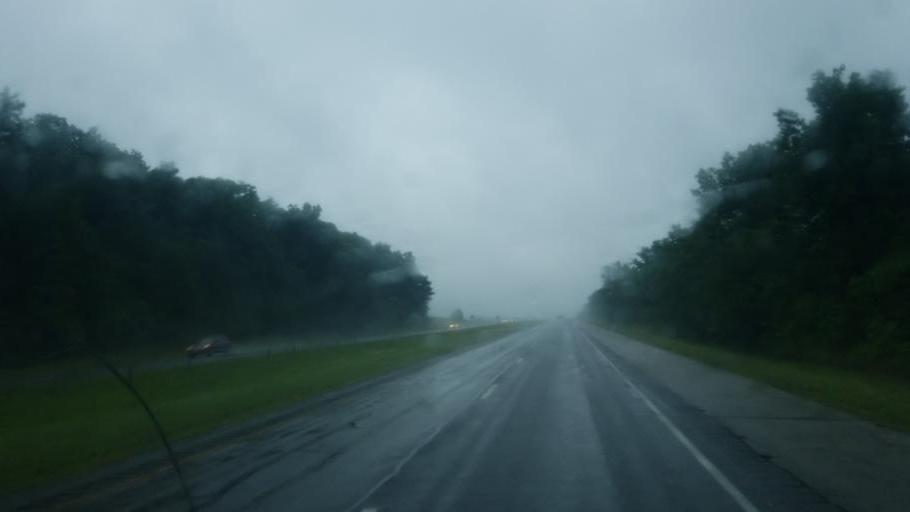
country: US
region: Indiana
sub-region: Grant County
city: Gas City
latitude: 40.5189
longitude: -85.5501
